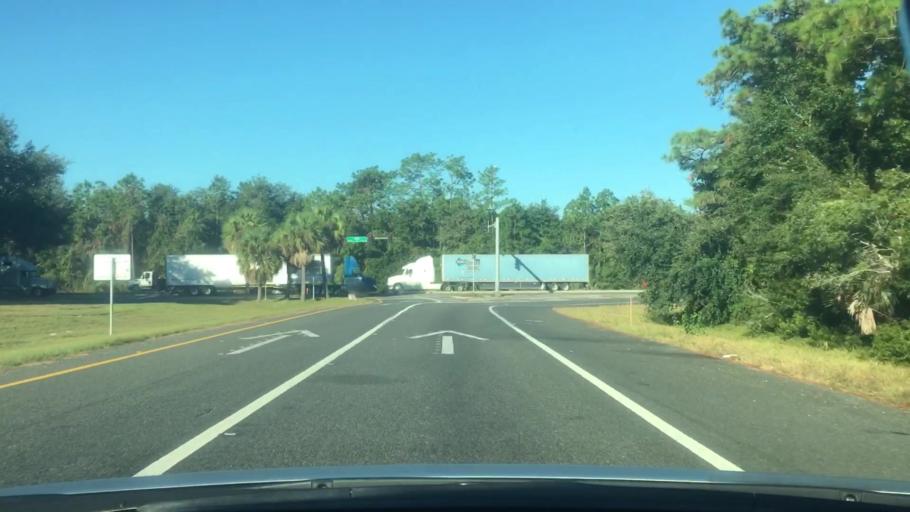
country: US
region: Florida
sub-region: Duval County
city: Jacksonville
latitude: 30.4347
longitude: -81.5789
